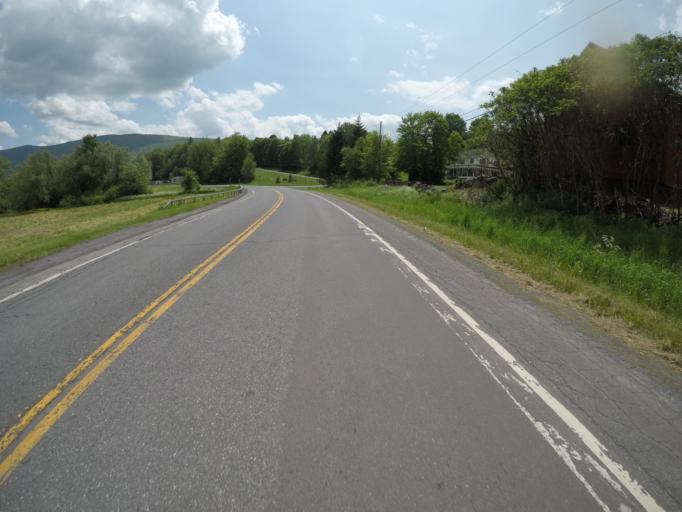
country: US
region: New York
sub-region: Delaware County
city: Stamford
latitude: 42.1604
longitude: -74.6242
